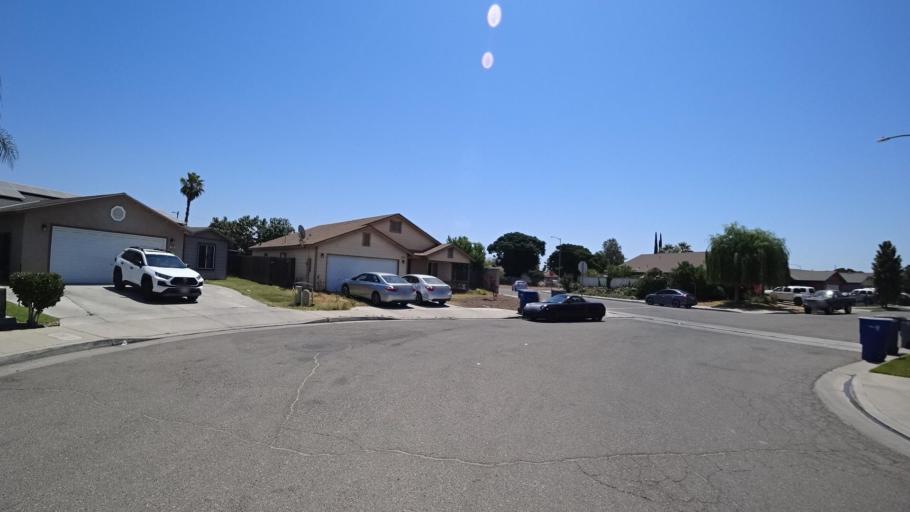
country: US
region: California
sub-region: Fresno County
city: West Park
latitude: 36.7101
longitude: -119.8162
